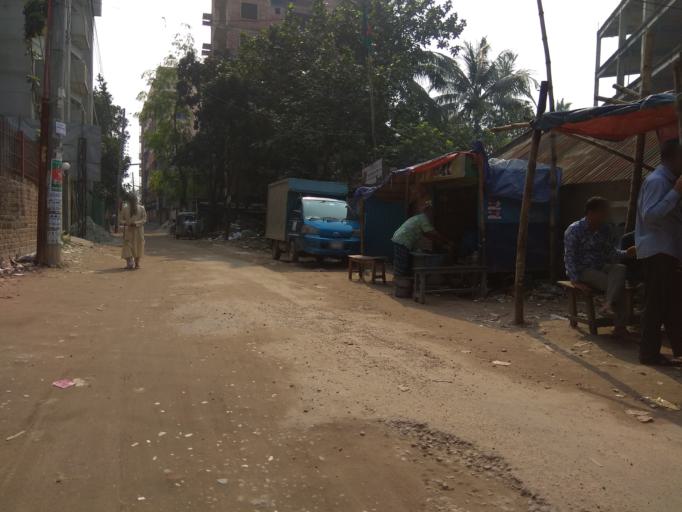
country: BD
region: Dhaka
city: Tungi
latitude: 23.8625
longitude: 90.3929
